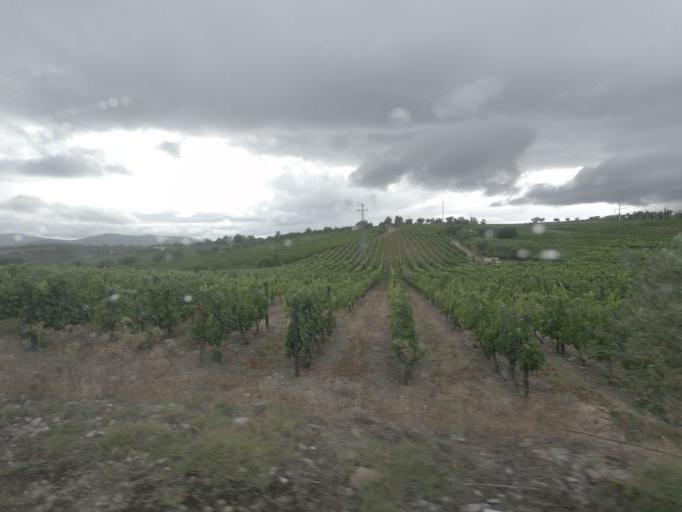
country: PT
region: Vila Real
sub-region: Sabrosa
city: Sabrosa
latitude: 41.2439
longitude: -7.4985
